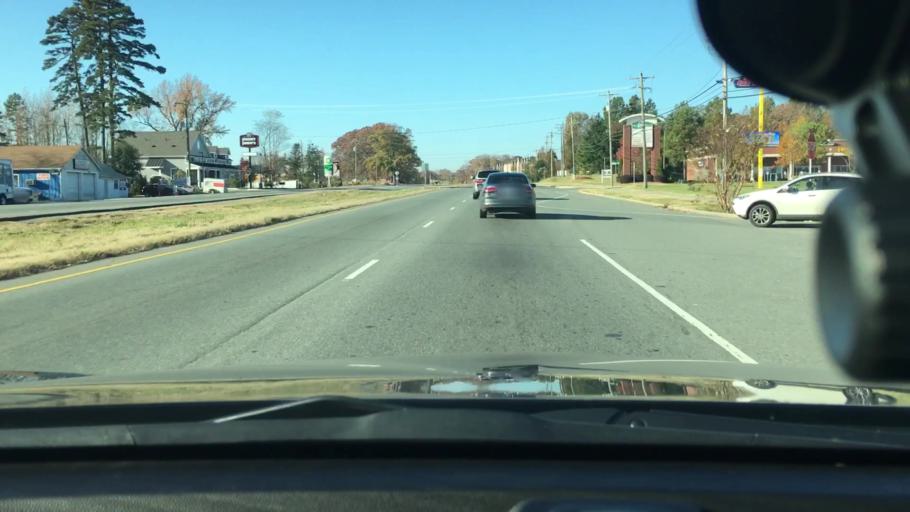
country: US
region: North Carolina
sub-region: Cabarrus County
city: Harrisburg
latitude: 35.3107
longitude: -80.7143
